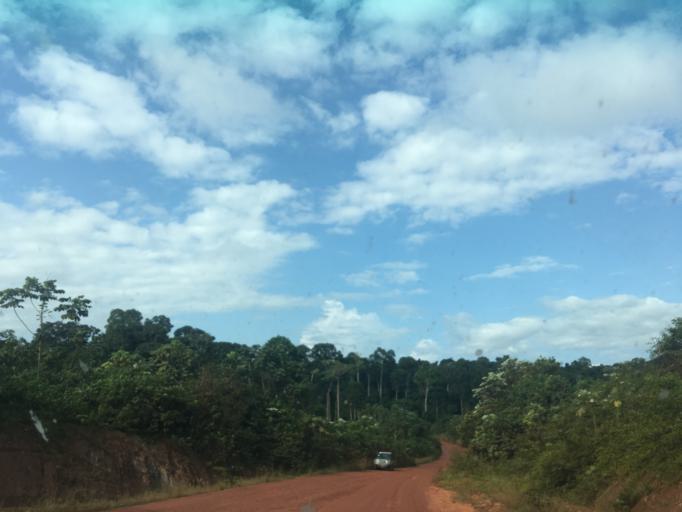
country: GH
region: Western
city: Wassa-Akropong
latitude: 5.9609
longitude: -2.4276
